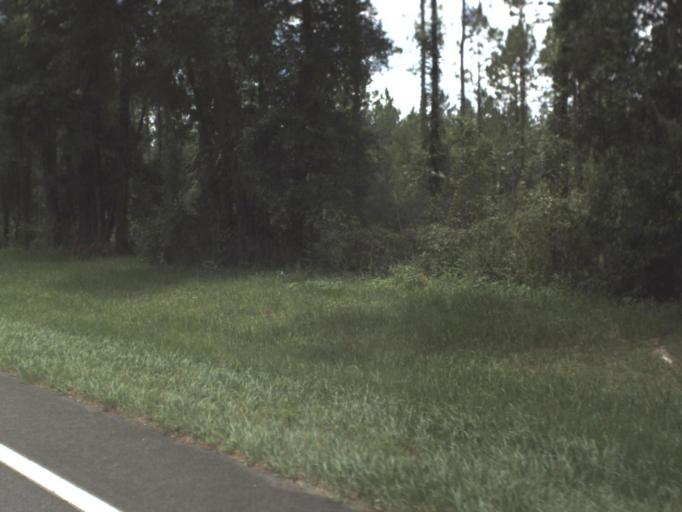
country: US
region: Florida
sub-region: Levy County
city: Williston
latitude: 29.4282
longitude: -82.4588
